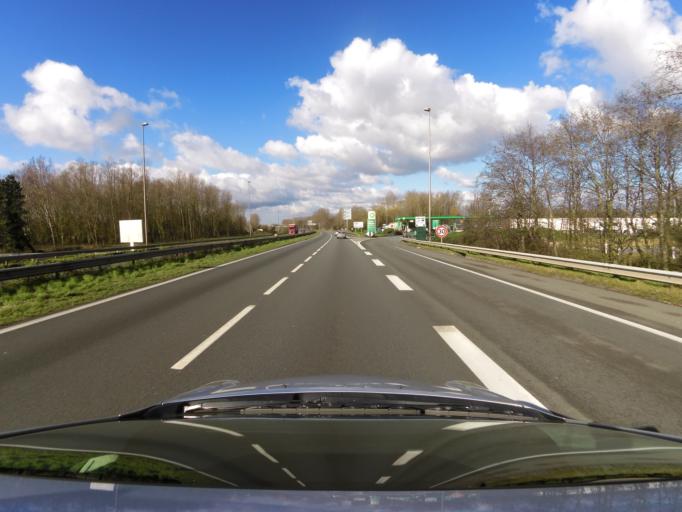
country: FR
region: Nord-Pas-de-Calais
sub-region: Departement du Nord
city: Grande-Synthe
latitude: 51.0038
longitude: 2.3061
